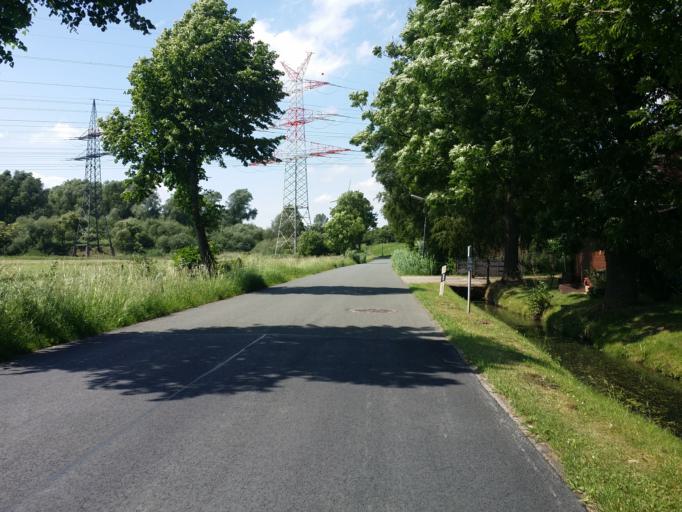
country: DE
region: Lower Saxony
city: Lemwerder
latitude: 53.1199
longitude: 8.6737
